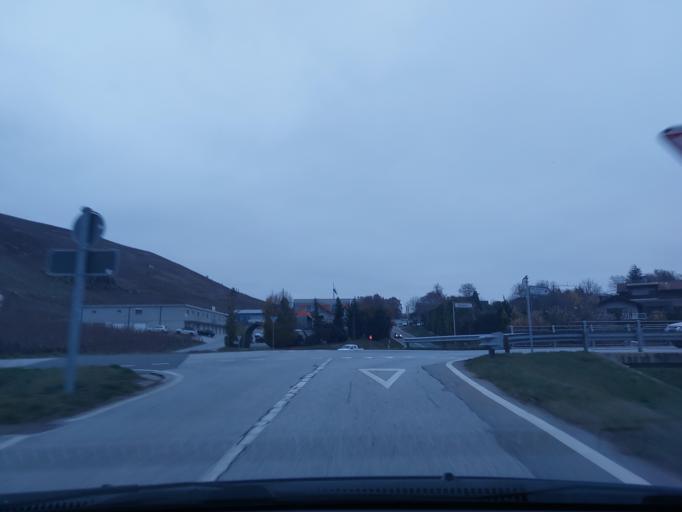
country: CH
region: Valais
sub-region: Sion District
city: Saviese
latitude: 46.2413
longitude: 7.3360
